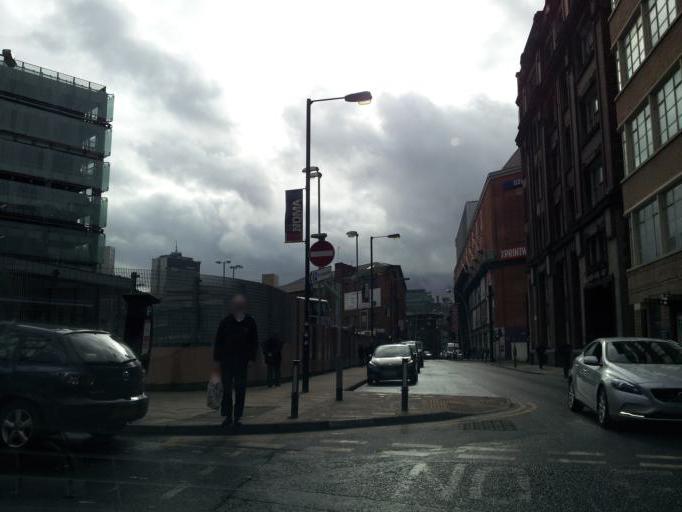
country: GB
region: England
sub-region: Manchester
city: Manchester
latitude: 53.4868
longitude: -2.2397
